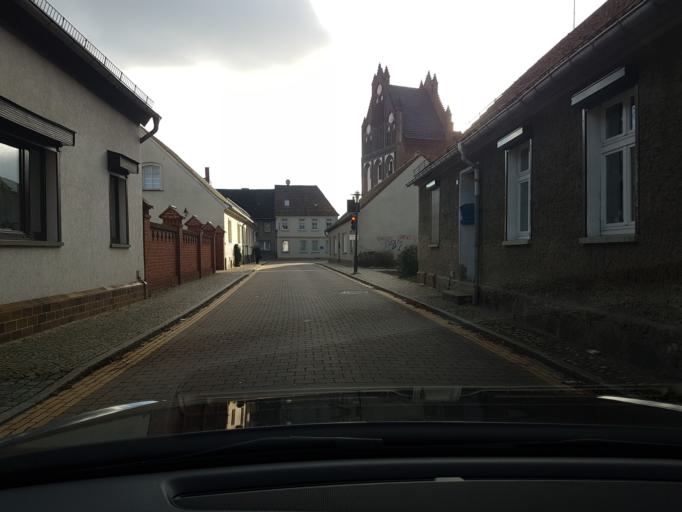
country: DE
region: Brandenburg
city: Gransee
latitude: 53.0078
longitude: 13.1531
